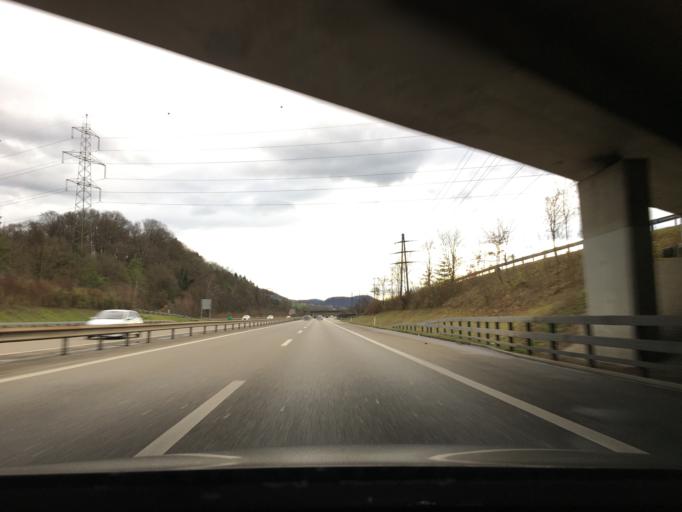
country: CH
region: Aargau
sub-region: Bezirk Laufenburg
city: Eiken
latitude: 47.5389
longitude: 7.9865
